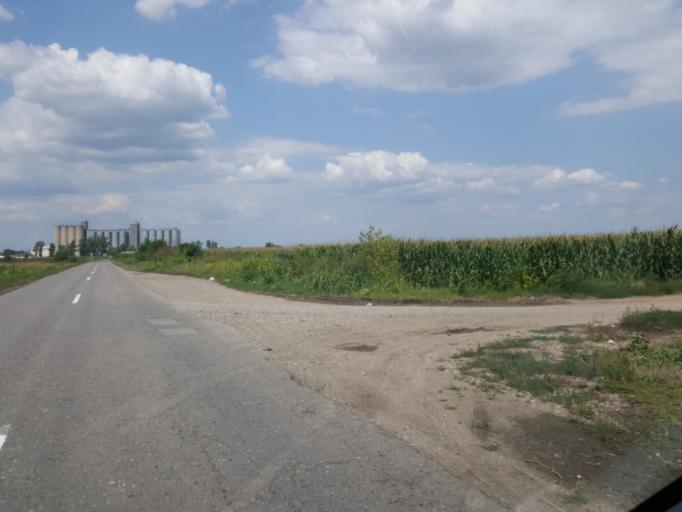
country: RS
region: Autonomna Pokrajina Vojvodina
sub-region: Sremski Okrug
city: Pecinci
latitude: 44.8777
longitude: 19.9613
